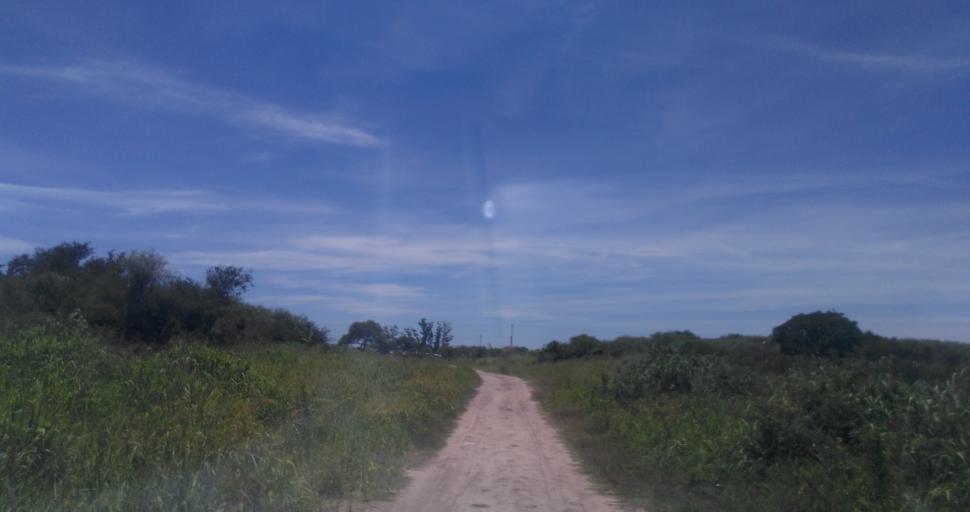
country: AR
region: Chaco
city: Fontana
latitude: -27.4258
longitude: -59.0463
